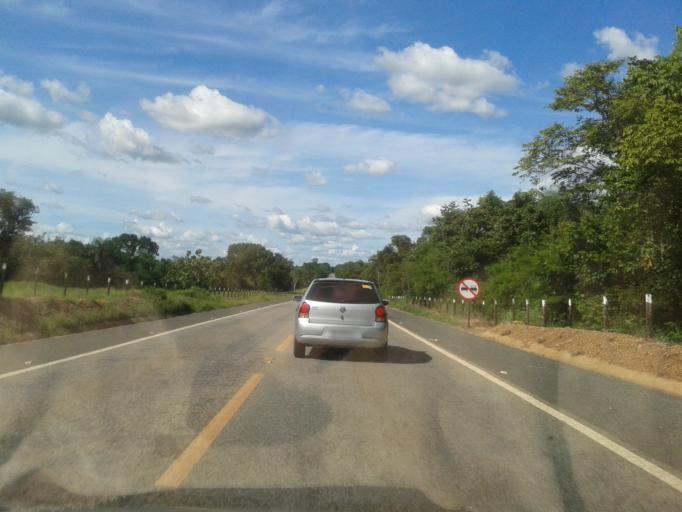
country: BR
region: Goias
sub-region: Mozarlandia
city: Mozarlandia
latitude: -15.0031
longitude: -50.5901
